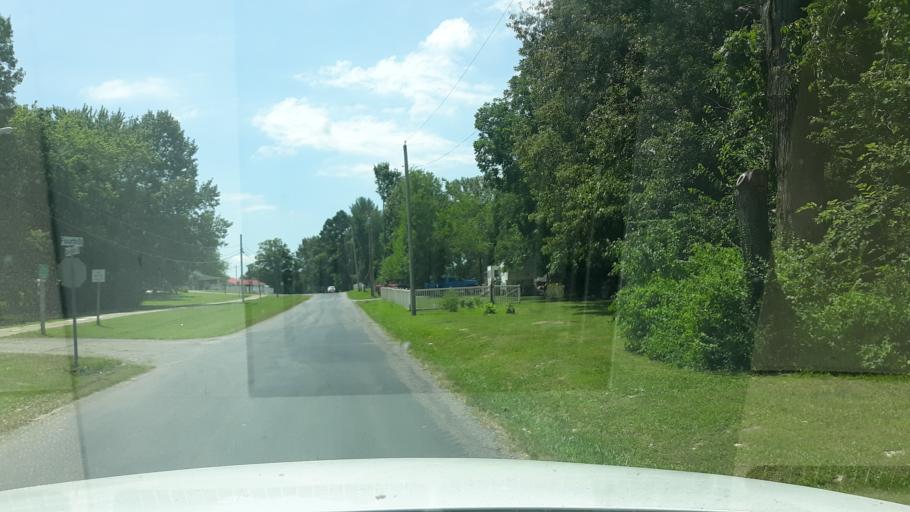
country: US
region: Illinois
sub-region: Saline County
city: Eldorado
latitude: 37.8071
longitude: -88.4337
